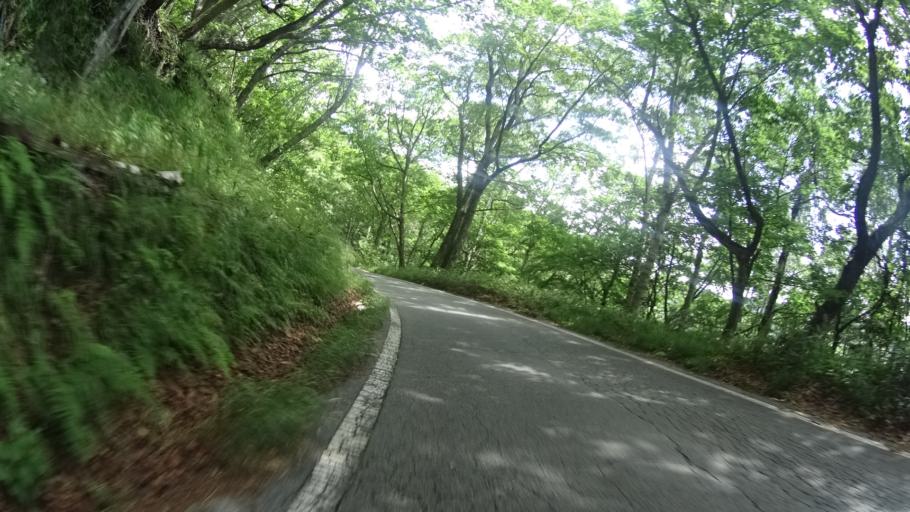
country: JP
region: Yamanashi
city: Enzan
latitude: 35.8284
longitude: 138.6395
